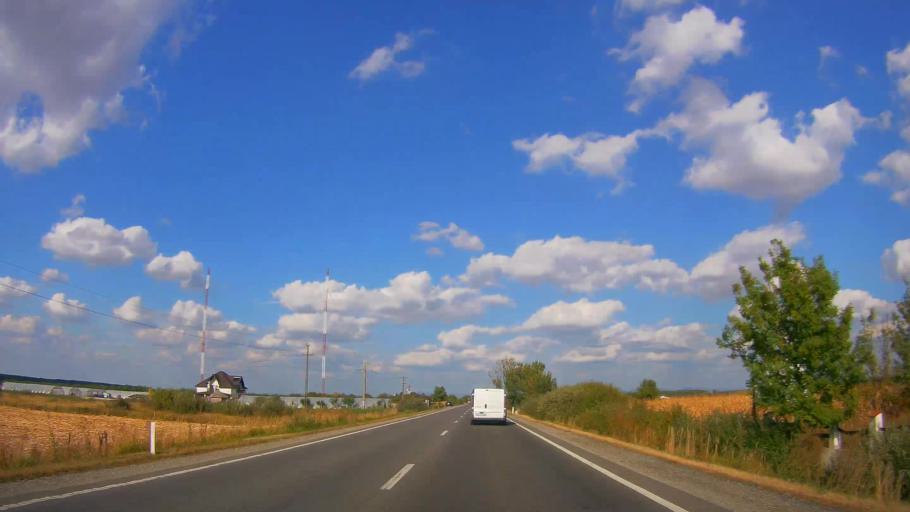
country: RO
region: Satu Mare
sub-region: Comuna Botiz
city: Botiz
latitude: 47.8499
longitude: 22.9717
